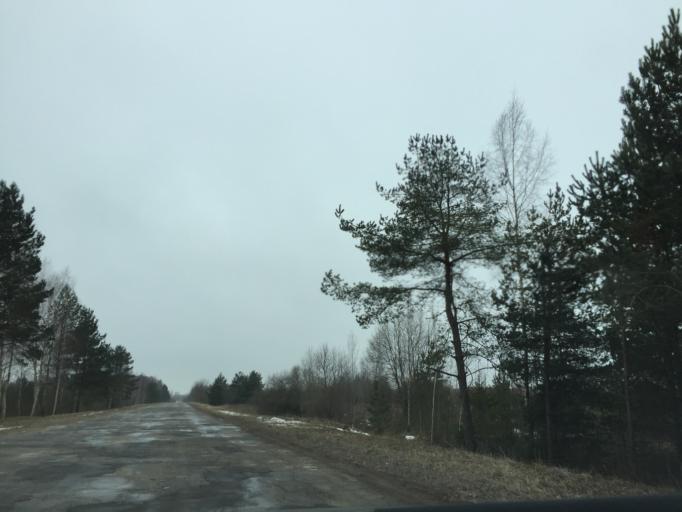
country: LV
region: Lecava
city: Iecava
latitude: 56.5781
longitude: 24.0759
